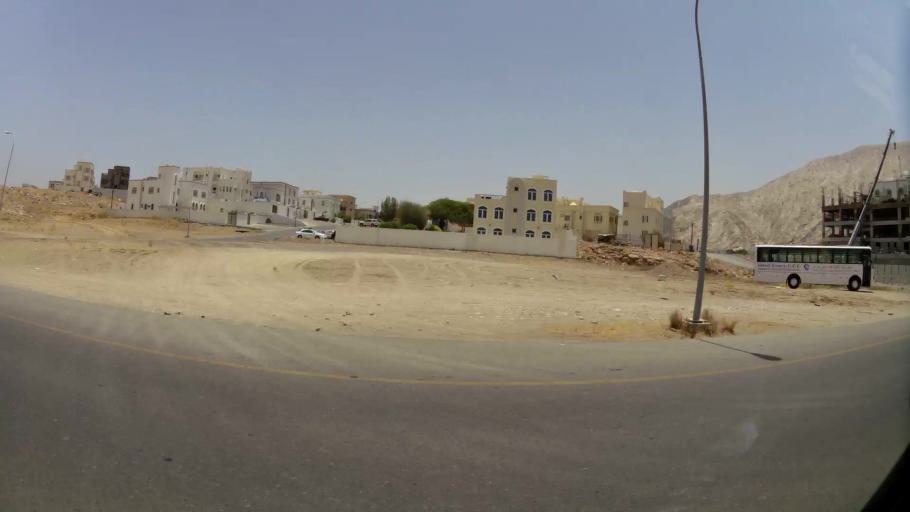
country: OM
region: Muhafazat Masqat
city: Bawshar
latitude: 23.5582
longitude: 58.4096
